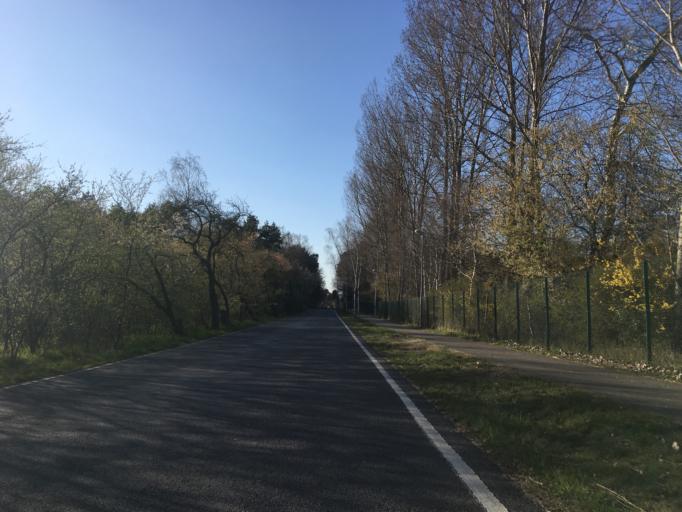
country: DE
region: Berlin
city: Buch
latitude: 52.6344
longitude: 13.5364
